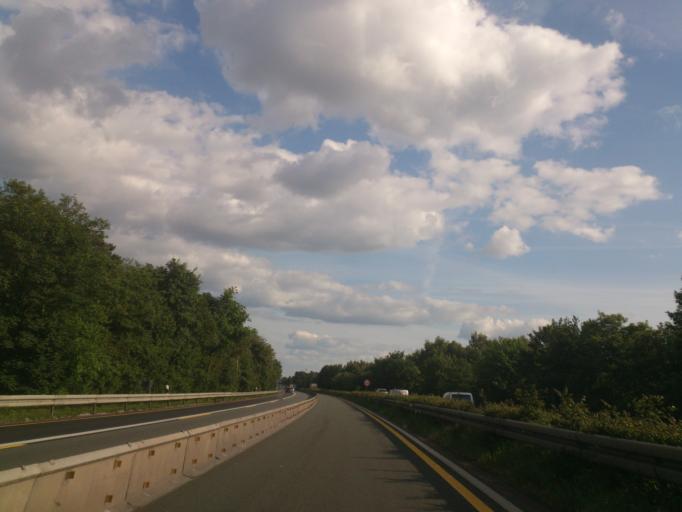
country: DE
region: North Rhine-Westphalia
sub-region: Regierungsbezirk Detmold
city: Hovelhof
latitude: 51.8061
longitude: 8.6985
